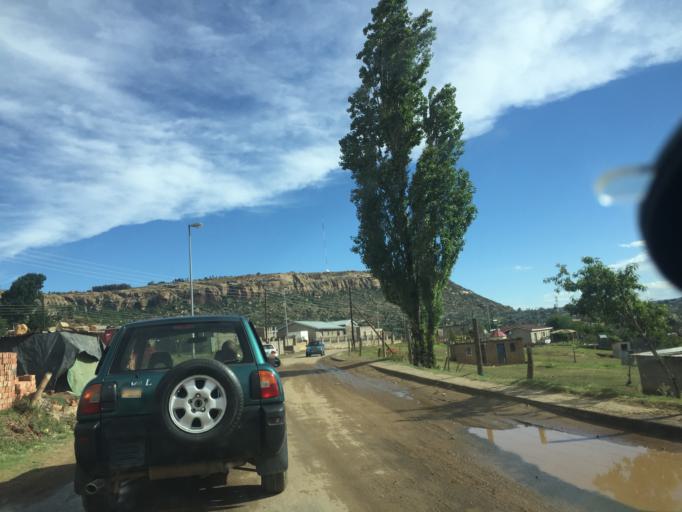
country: LS
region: Maseru
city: Maseru
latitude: -29.3122
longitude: 27.5383
